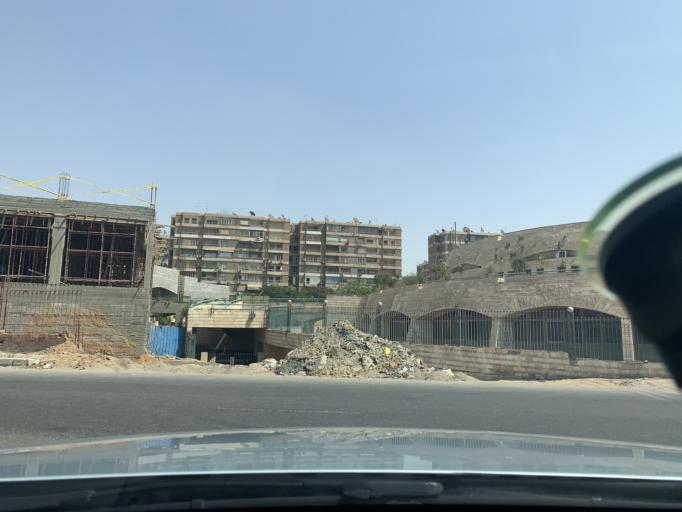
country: EG
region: Muhafazat al Qalyubiyah
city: Al Khankah
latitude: 30.1107
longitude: 31.3758
